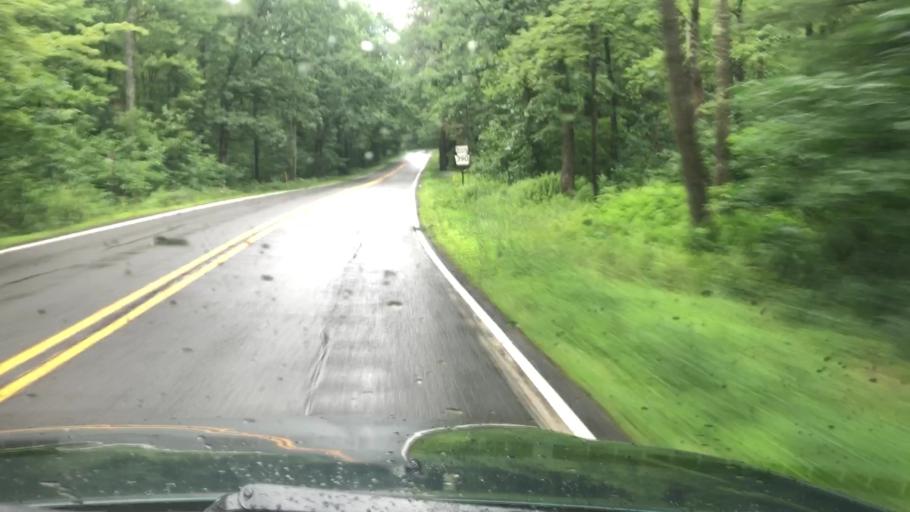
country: US
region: Pennsylvania
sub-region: Wayne County
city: Hawley
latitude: 41.3495
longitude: -75.2124
